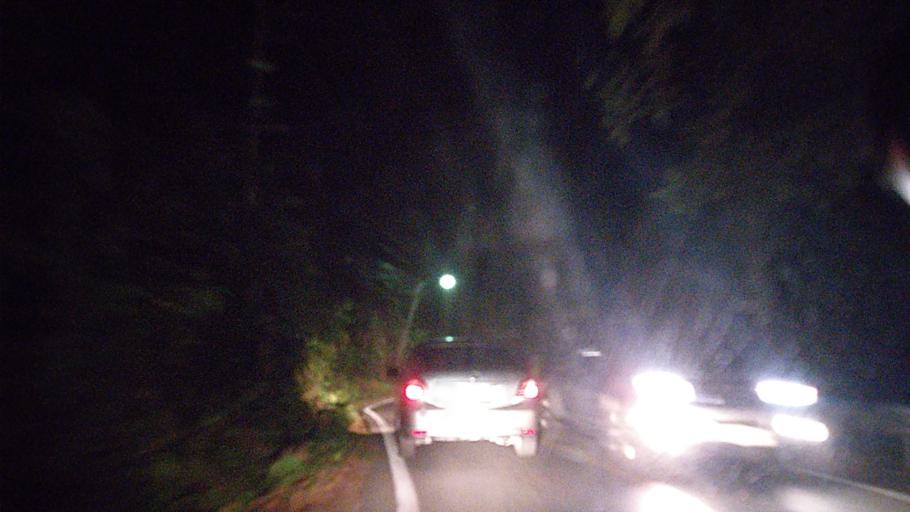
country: TH
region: Trat
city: Ko Chang Tai
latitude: 12.0141
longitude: 102.2905
